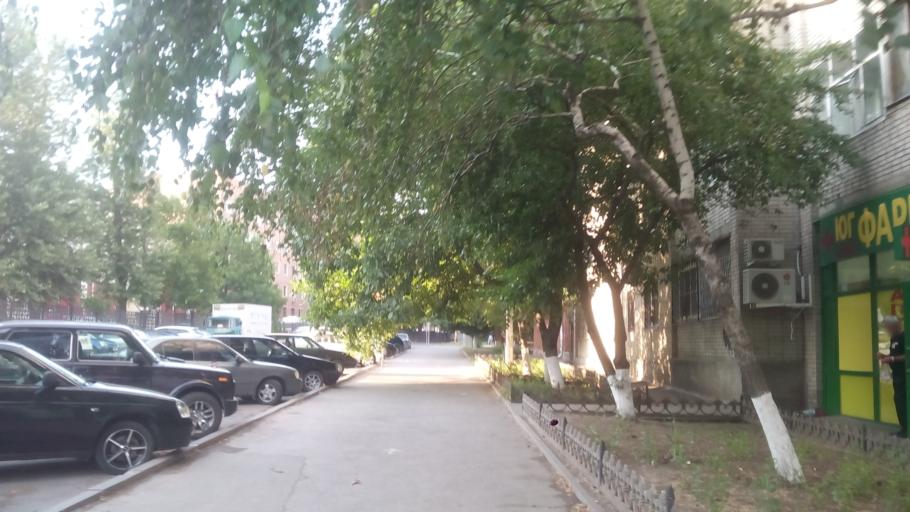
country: RU
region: Rostov
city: Imeni Chkalova
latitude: 47.2575
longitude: 39.7692
